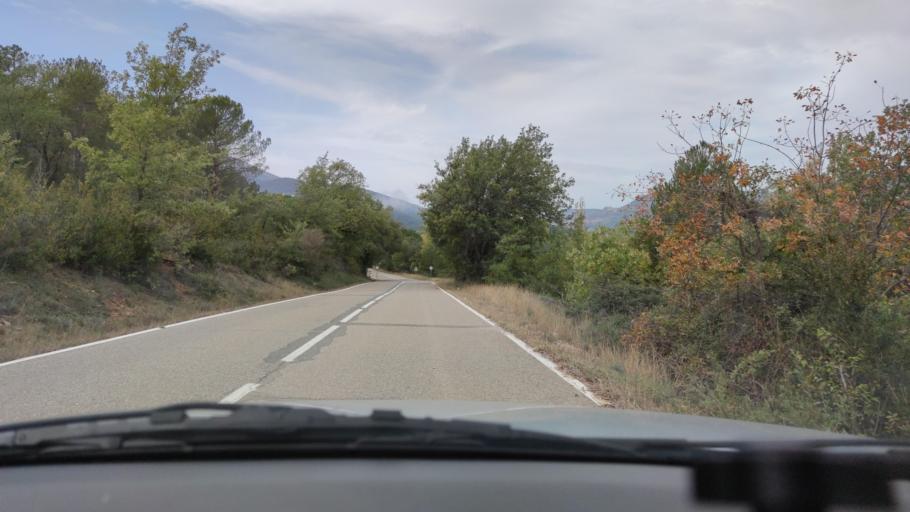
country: ES
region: Catalonia
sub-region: Provincia de Lleida
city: Llimiana
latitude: 42.0603
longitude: 0.8985
